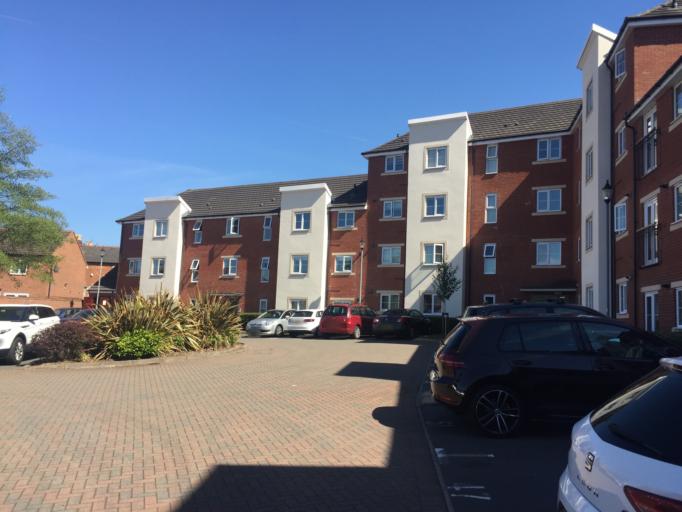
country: GB
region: England
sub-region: Sandwell
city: Smethwick
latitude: 52.4835
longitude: -1.9516
